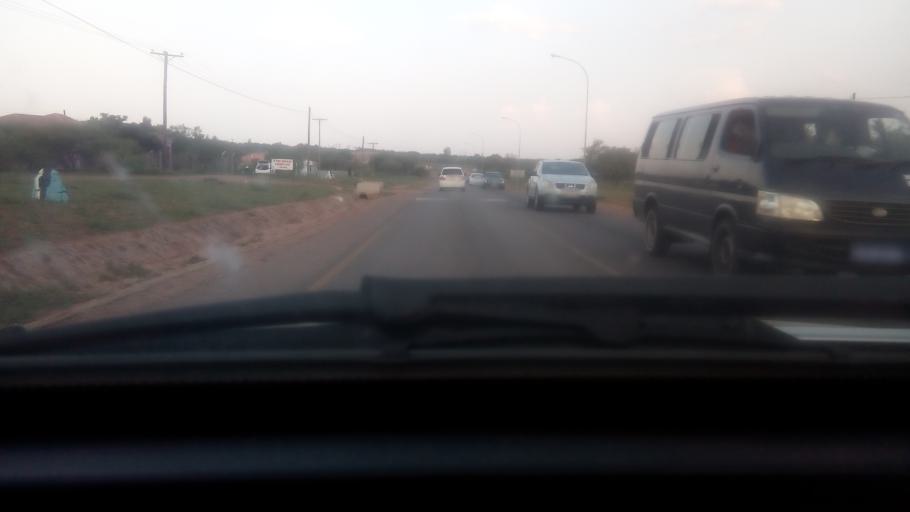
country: BW
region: Kgatleng
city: Bokaa
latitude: -24.4331
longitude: 26.0314
